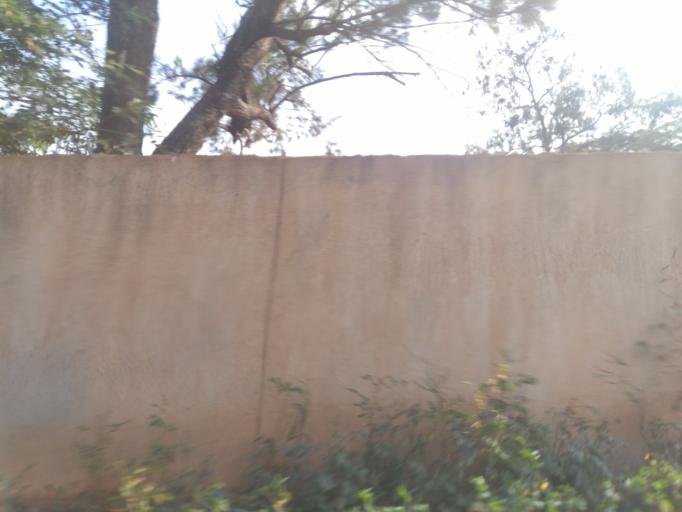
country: UG
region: Eastern Region
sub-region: Jinja District
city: Jinja
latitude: 0.4161
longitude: 33.2167
